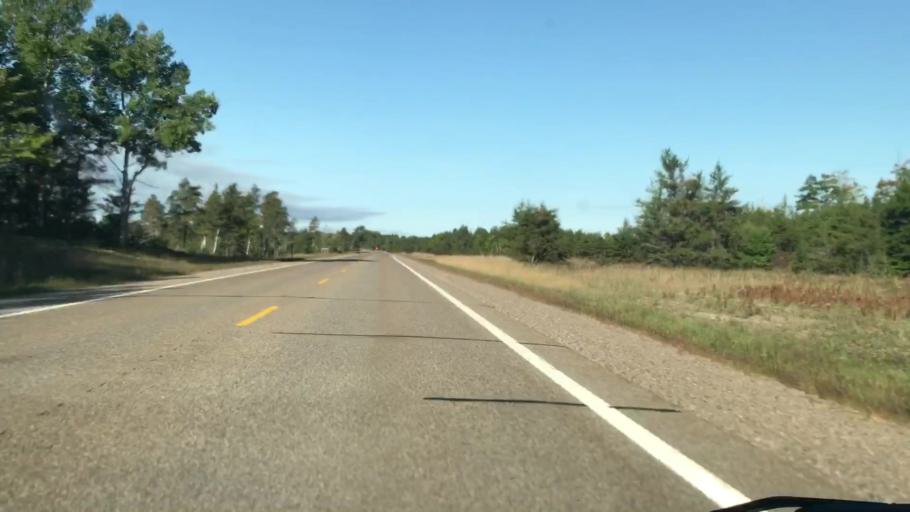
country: US
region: Michigan
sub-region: Mackinac County
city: Saint Ignace
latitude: 46.3584
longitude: -84.8754
